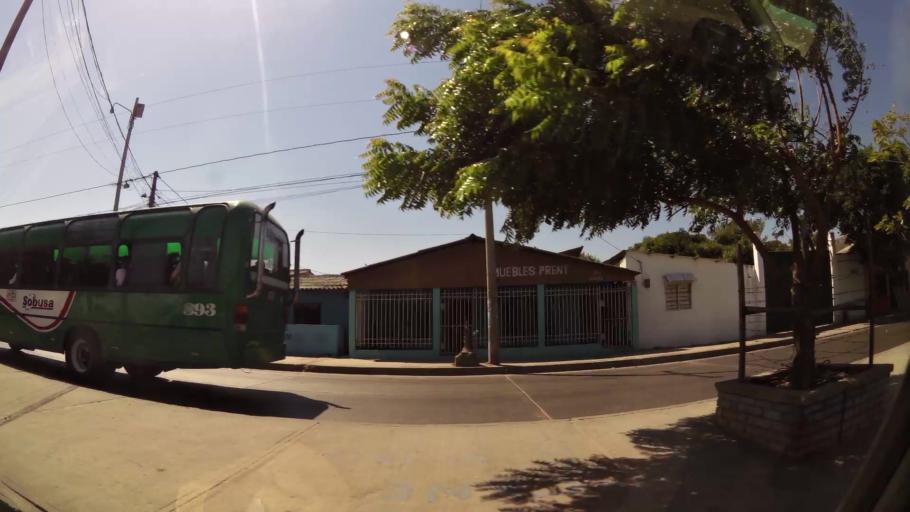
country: CO
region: Atlantico
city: Barranquilla
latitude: 10.9588
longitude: -74.7747
